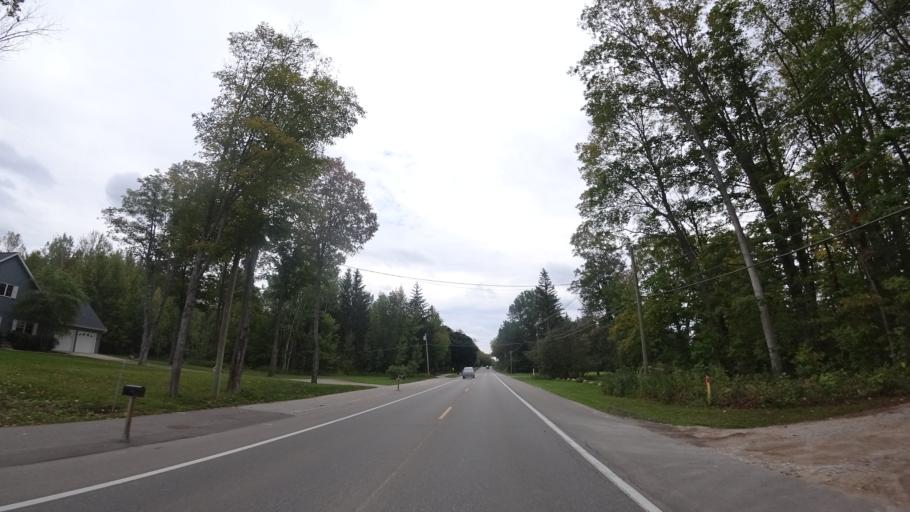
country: US
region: Michigan
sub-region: Emmet County
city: Harbor Springs
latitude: 45.4310
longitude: -84.9328
